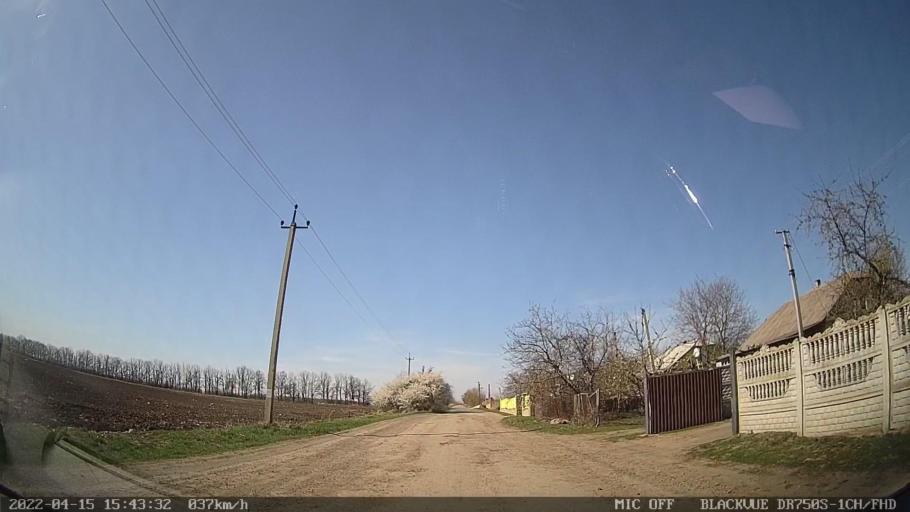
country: MD
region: Raionul Ocnita
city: Otaci
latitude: 48.3656
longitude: 27.9259
